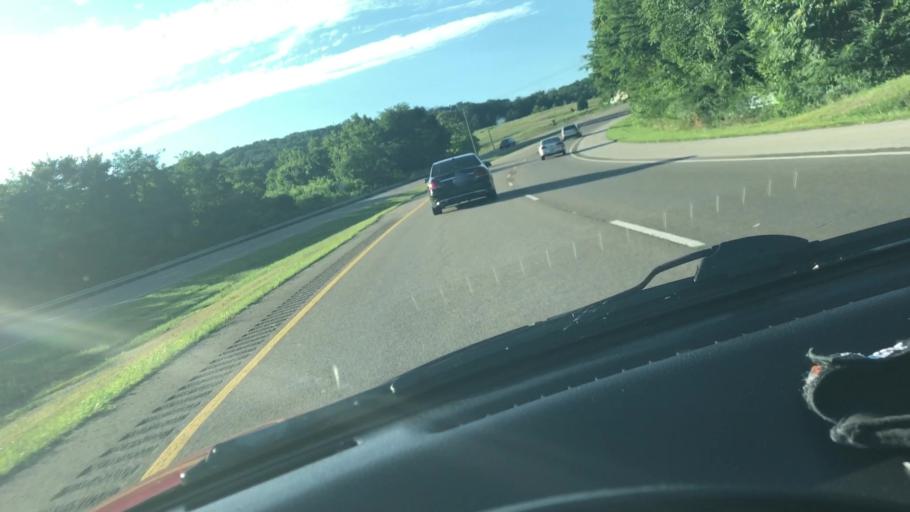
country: US
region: Tennessee
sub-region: Jefferson County
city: Jefferson City
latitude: 36.0646
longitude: -83.4794
